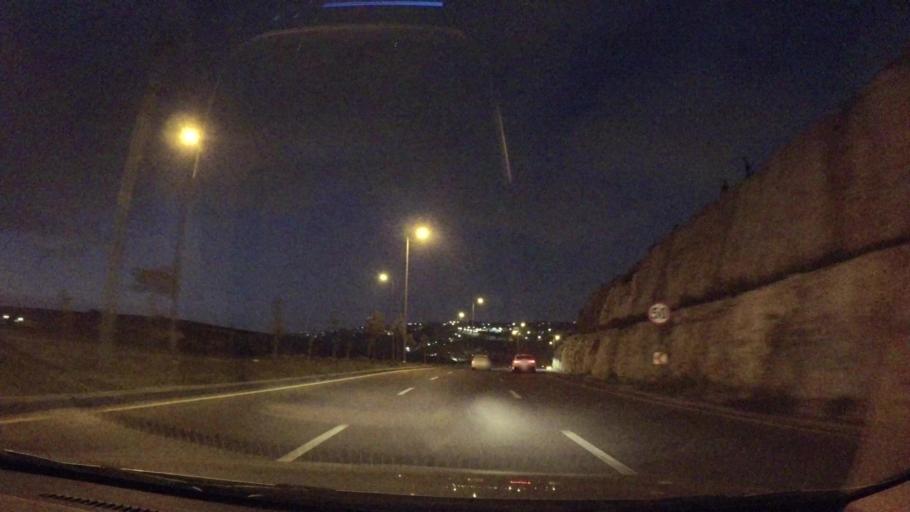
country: JO
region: Amman
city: Al Bunayyat ash Shamaliyah
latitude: 31.9241
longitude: 35.8783
